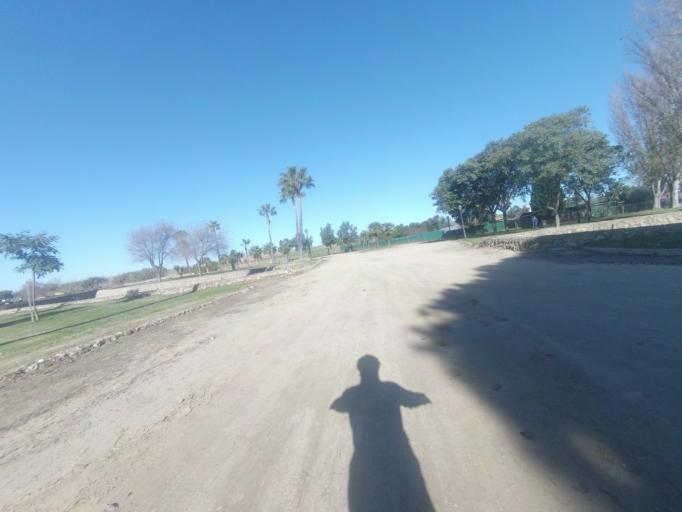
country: ES
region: Andalusia
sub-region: Provincia de Huelva
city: Palos de la Frontera
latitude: 37.2325
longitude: -6.8903
